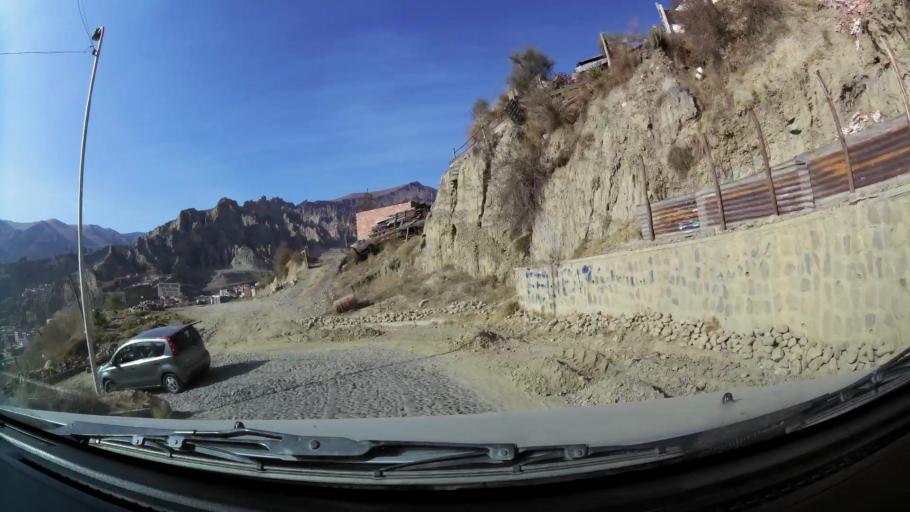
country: BO
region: La Paz
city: La Paz
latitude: -16.5071
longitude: -68.0810
